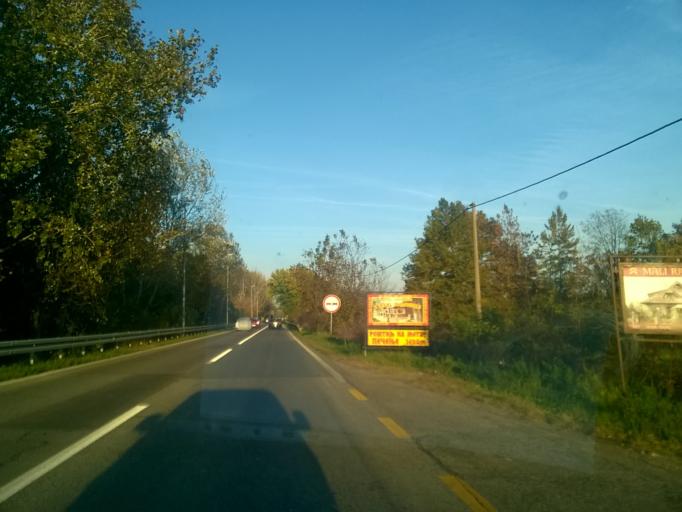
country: RS
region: Autonomna Pokrajina Vojvodina
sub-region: Juznobanatski Okrug
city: Pancevo
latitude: 44.8666
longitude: 20.5907
